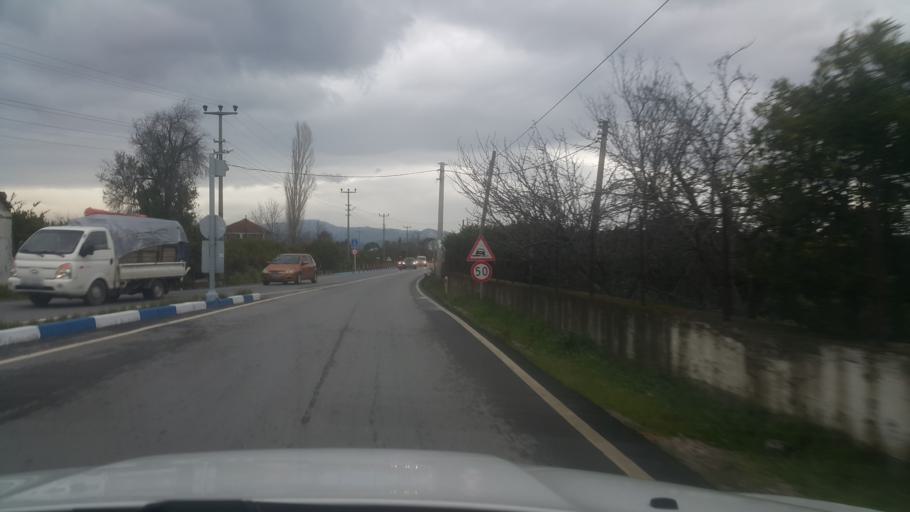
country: TR
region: Izmir
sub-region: Seferihisar
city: Seferhisar
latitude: 38.1883
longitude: 26.8084
